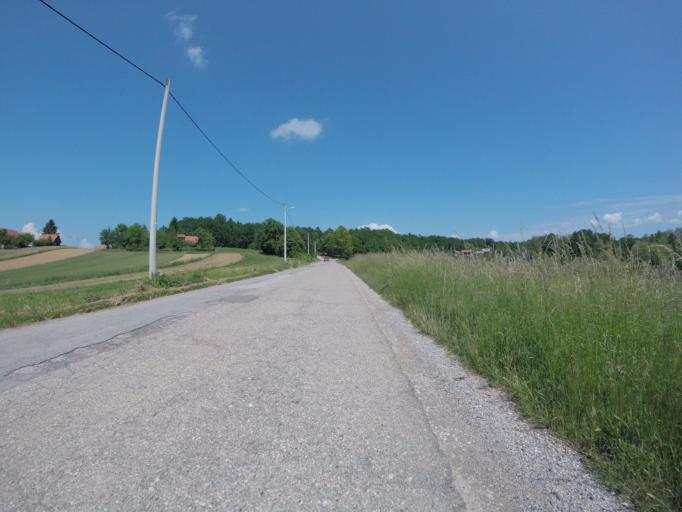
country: HR
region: Grad Zagreb
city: Strmec
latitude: 45.5780
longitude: 15.9435
